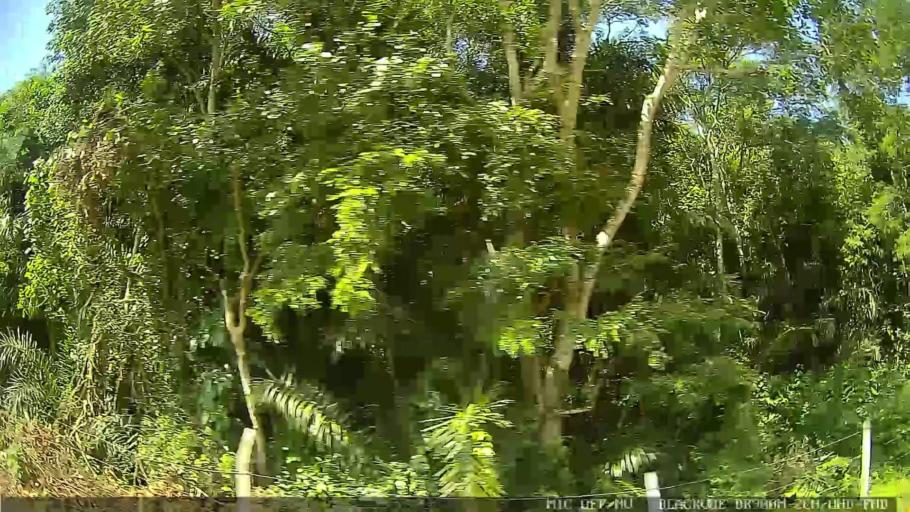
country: BR
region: Sao Paulo
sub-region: Guaruja
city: Guaruja
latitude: -24.0120
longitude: -46.3008
